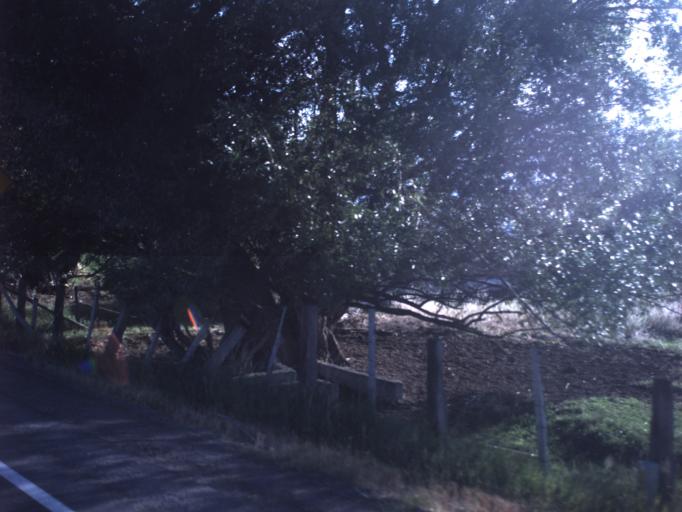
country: US
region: Utah
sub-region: Sanpete County
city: Mount Pleasant
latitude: 39.5836
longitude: -111.4538
